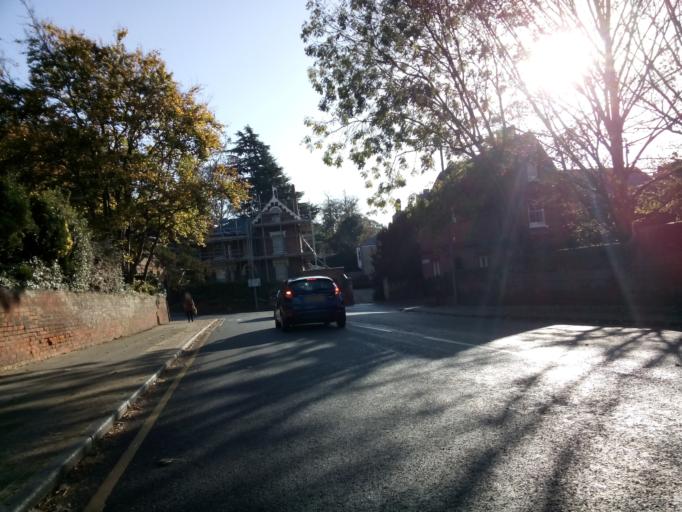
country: GB
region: England
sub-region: Suffolk
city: Ipswich
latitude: 52.0627
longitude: 1.1508
